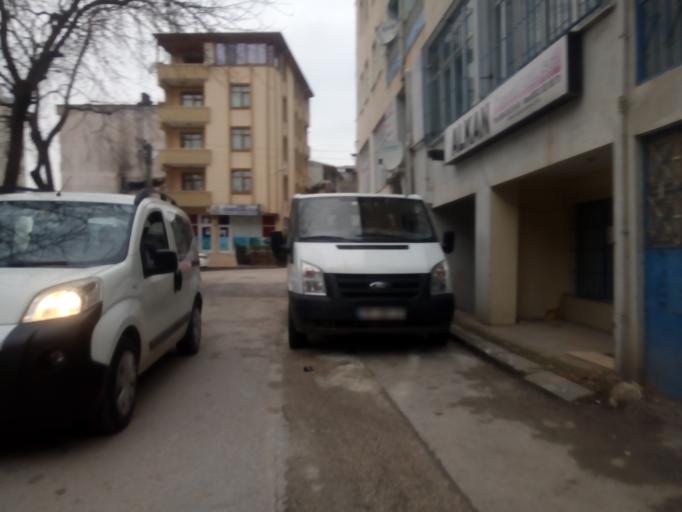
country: TR
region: Bursa
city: Niluefer
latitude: 40.2534
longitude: 28.9608
